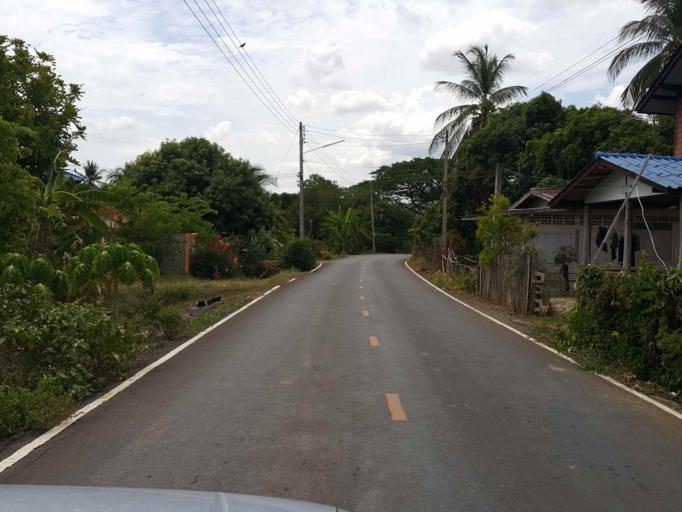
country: TH
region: Sukhothai
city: Thung Saliam
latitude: 17.3266
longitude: 99.5595
